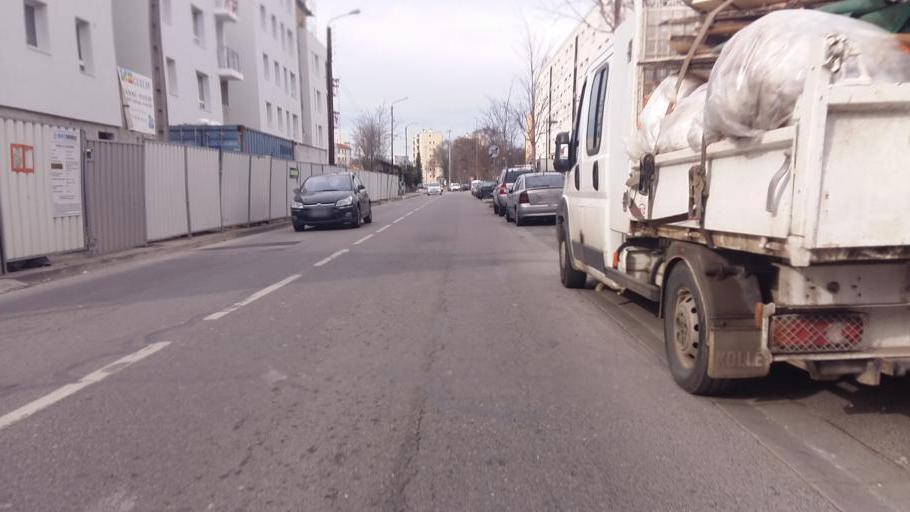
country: FR
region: Rhone-Alpes
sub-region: Departement du Rhone
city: Villeurbanne
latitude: 45.7802
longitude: 4.8917
